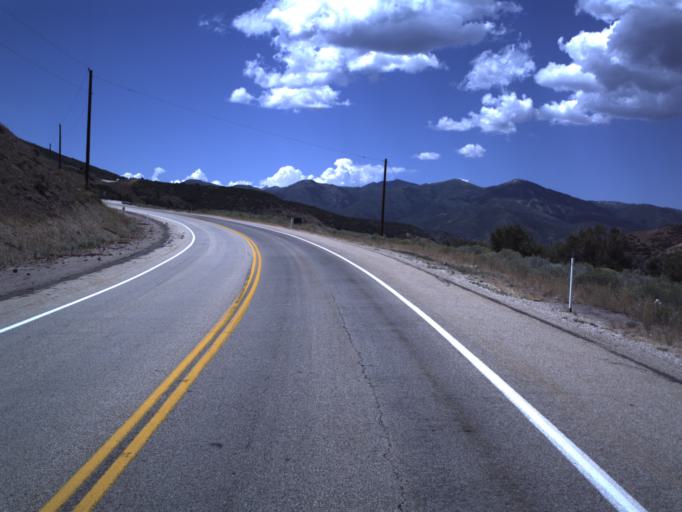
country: US
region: Utah
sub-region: Summit County
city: Francis
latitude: 40.6015
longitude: -111.3341
